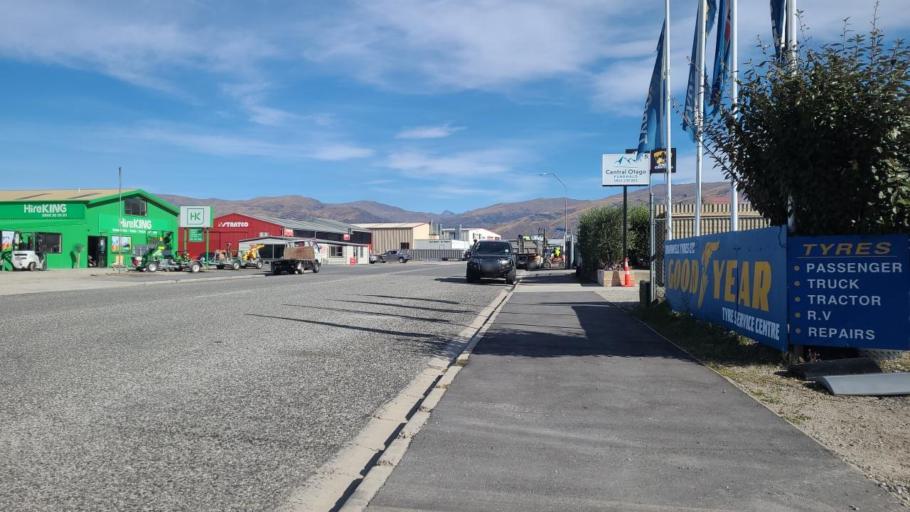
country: NZ
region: Otago
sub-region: Queenstown-Lakes District
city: Wanaka
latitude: -45.0495
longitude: 169.1940
